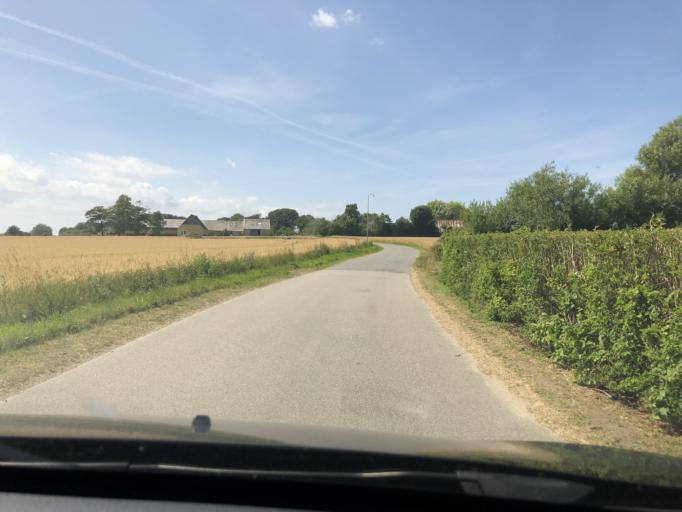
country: DK
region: South Denmark
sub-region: AEro Kommune
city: AEroskobing
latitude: 54.8914
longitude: 10.3043
